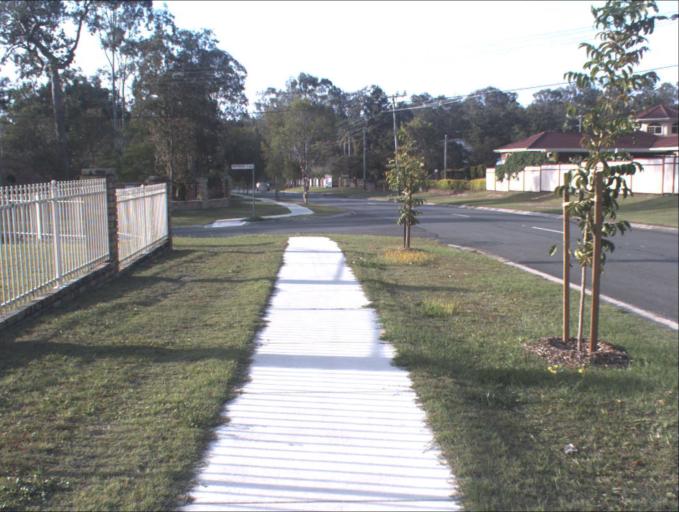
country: AU
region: Queensland
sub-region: Logan
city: Park Ridge South
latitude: -27.6751
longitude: 153.0138
